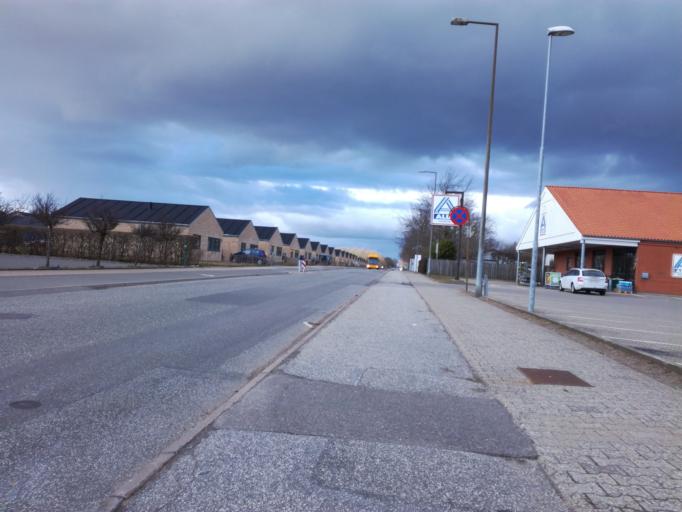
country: DK
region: South Denmark
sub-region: Fredericia Kommune
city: Fredericia
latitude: 55.5813
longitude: 9.7672
